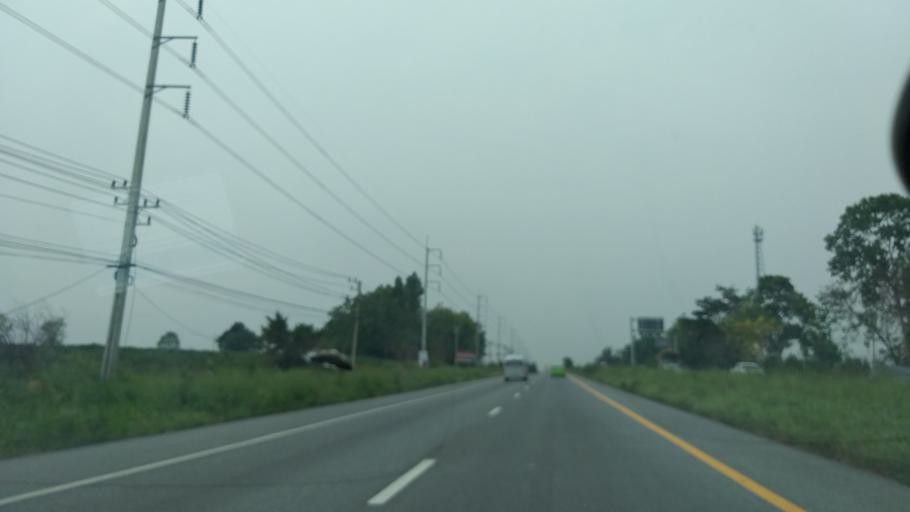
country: TH
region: Chon Buri
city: Ko Chan
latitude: 13.4281
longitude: 101.2827
